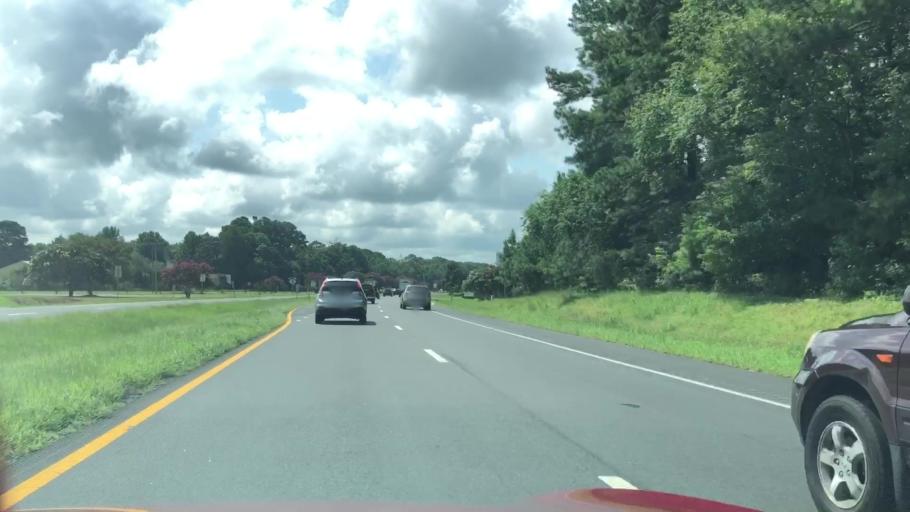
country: US
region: Virginia
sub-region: Northampton County
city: Exmore
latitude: 37.5165
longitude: -75.8322
